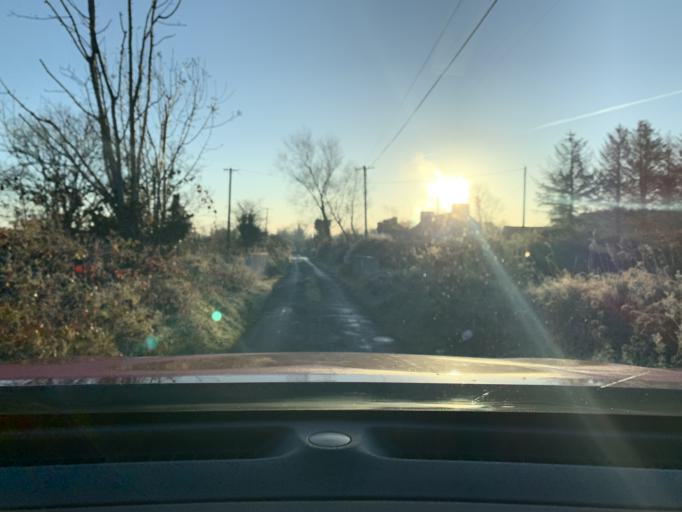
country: IE
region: Connaught
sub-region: Sligo
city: Ballymote
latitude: 53.9869
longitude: -8.5259
